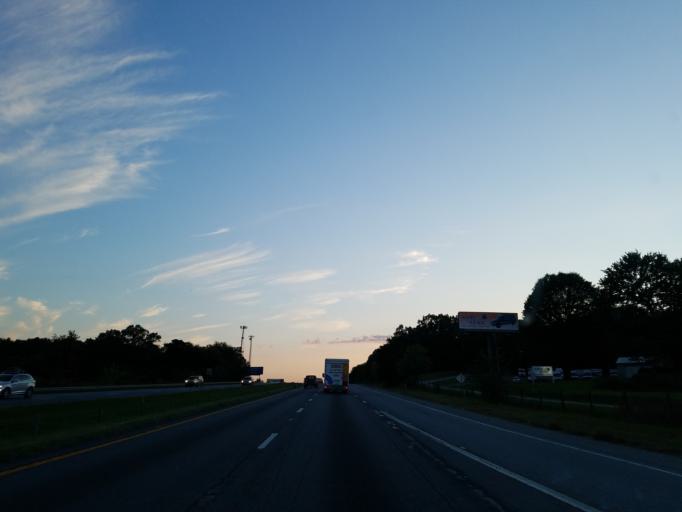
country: US
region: South Carolina
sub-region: Spartanburg County
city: Cowpens
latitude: 35.0709
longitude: -81.7624
